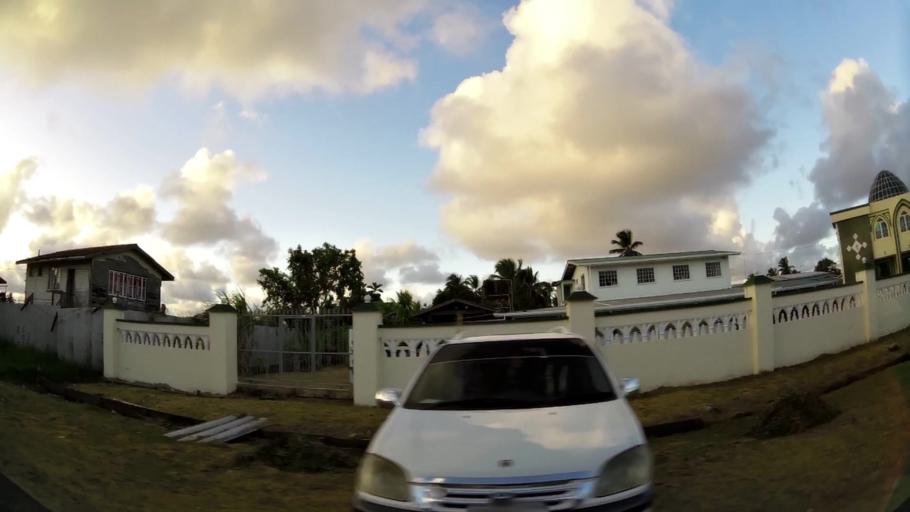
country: GY
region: Demerara-Mahaica
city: Georgetown
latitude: 6.8143
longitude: -58.1022
